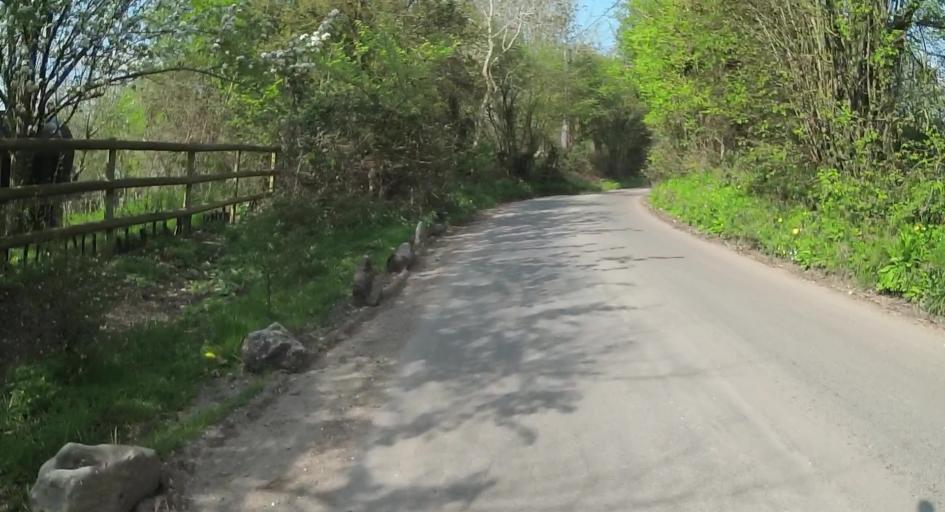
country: GB
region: England
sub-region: Hampshire
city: Tadley
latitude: 51.3868
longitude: -1.1281
